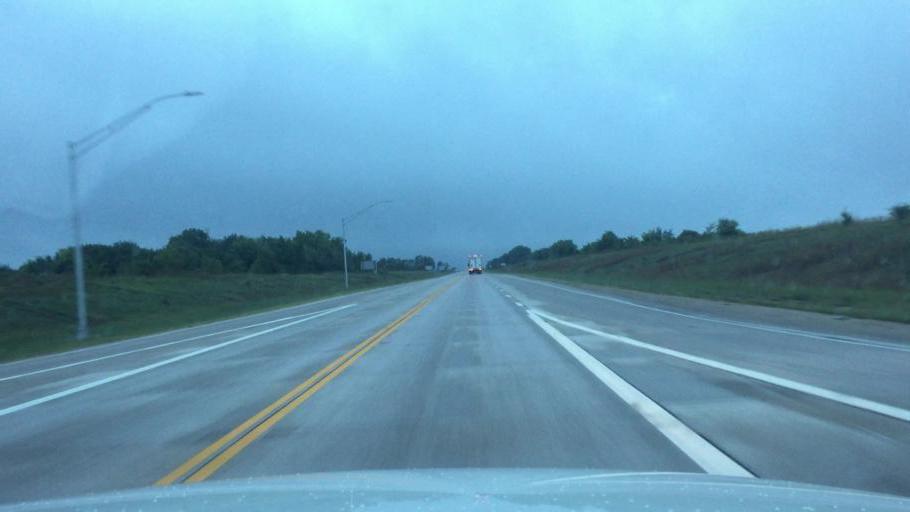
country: US
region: Kansas
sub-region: Neosho County
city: Chanute
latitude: 37.6434
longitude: -95.4797
